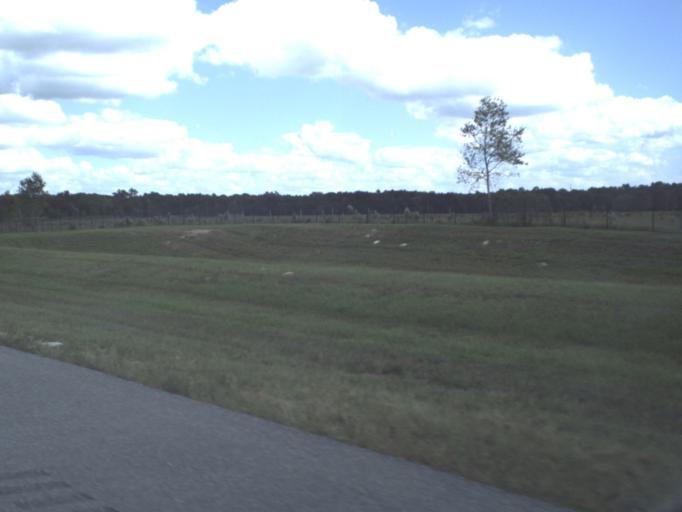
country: US
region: Florida
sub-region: Pasco County
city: Shady Hills
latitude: 28.4075
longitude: -82.5097
